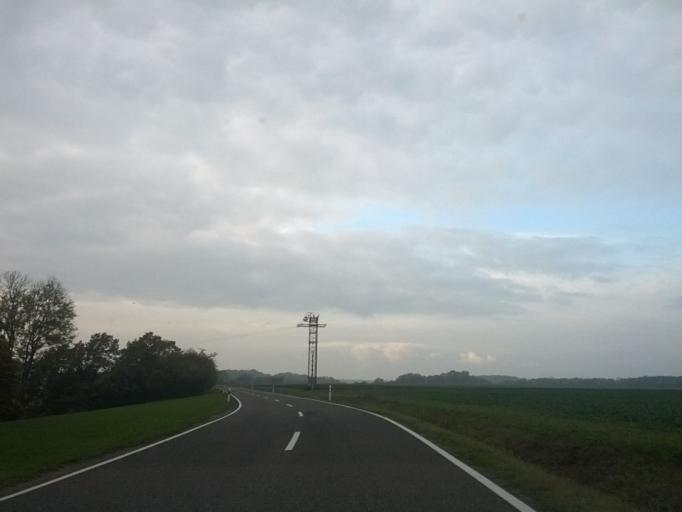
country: DE
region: Hesse
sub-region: Regierungsbezirk Kassel
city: Herleshausen
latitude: 51.0407
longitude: 10.1565
